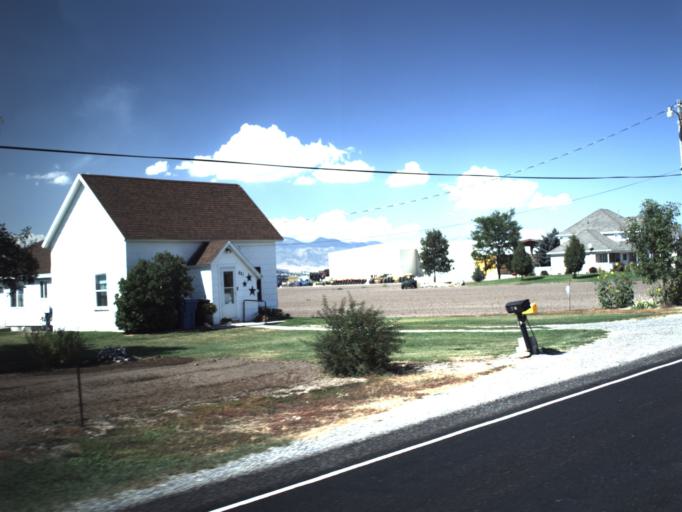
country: US
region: Utah
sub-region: Cache County
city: Lewiston
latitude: 41.9877
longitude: -111.8764
